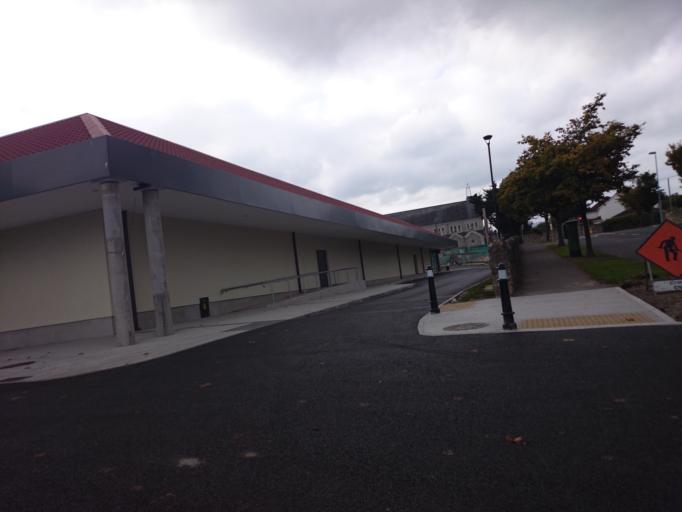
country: IE
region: Leinster
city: Shankill
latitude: 53.2343
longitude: -6.1217
